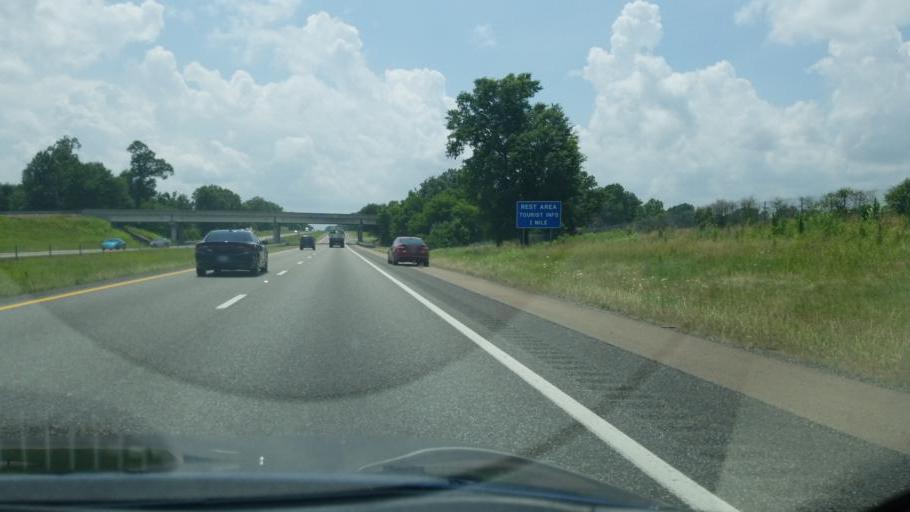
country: US
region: Tennessee
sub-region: Madison County
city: Jackson
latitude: 35.6337
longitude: -88.9475
